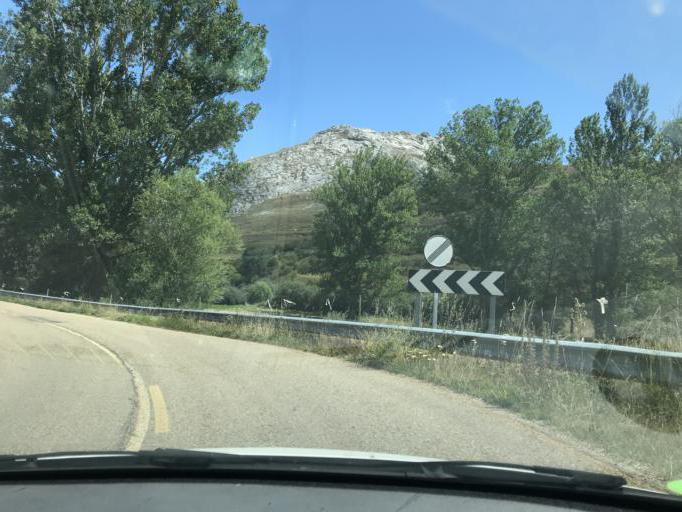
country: ES
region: Castille and Leon
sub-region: Provincia de Palencia
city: Polentinos
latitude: 43.0117
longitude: -4.4912
